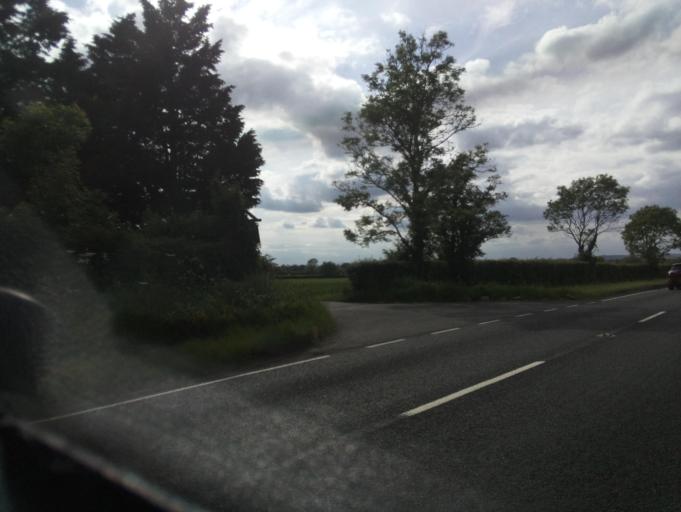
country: GB
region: England
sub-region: Worcestershire
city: Broadway
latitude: 52.0766
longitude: -1.8417
